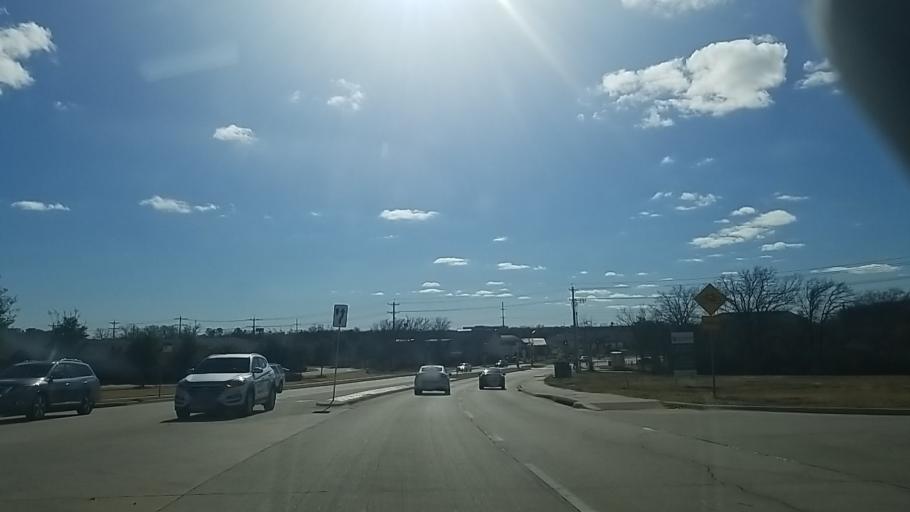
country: US
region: Texas
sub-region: Denton County
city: Corinth
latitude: 33.1867
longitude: -97.0958
